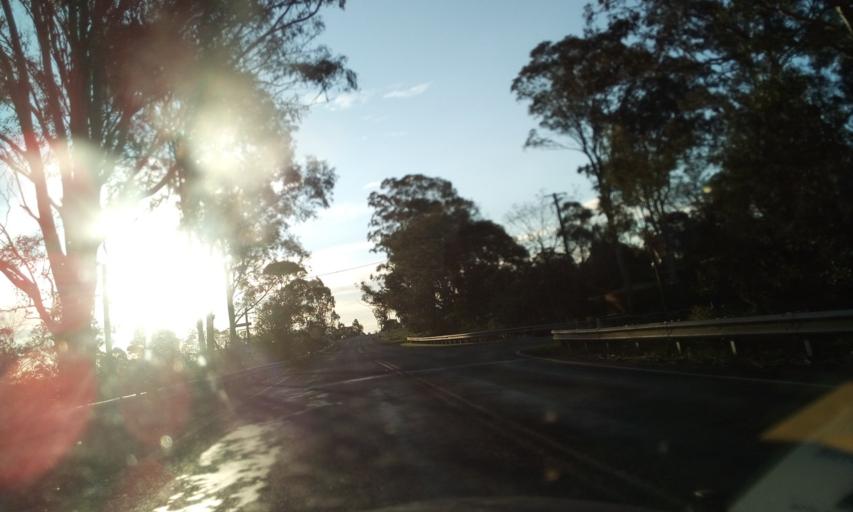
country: AU
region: New South Wales
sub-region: Wollondilly
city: Douglas Park
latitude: -34.2406
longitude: 150.7028
